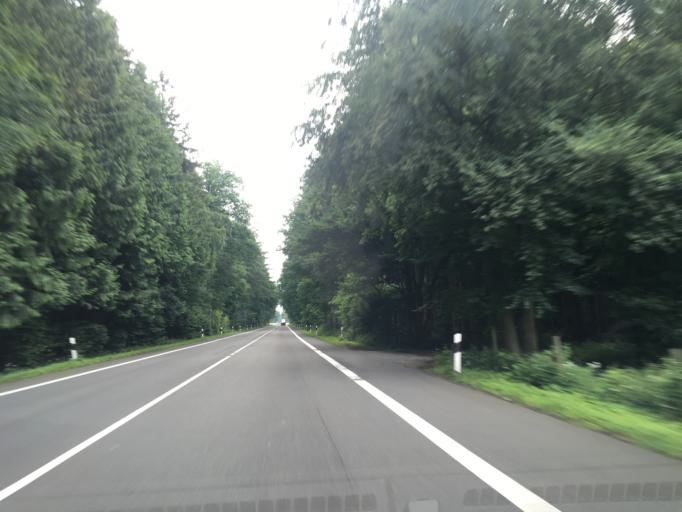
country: DE
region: North Rhine-Westphalia
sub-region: Regierungsbezirk Munster
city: Neuenkirchen
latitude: 52.1961
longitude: 7.3683
